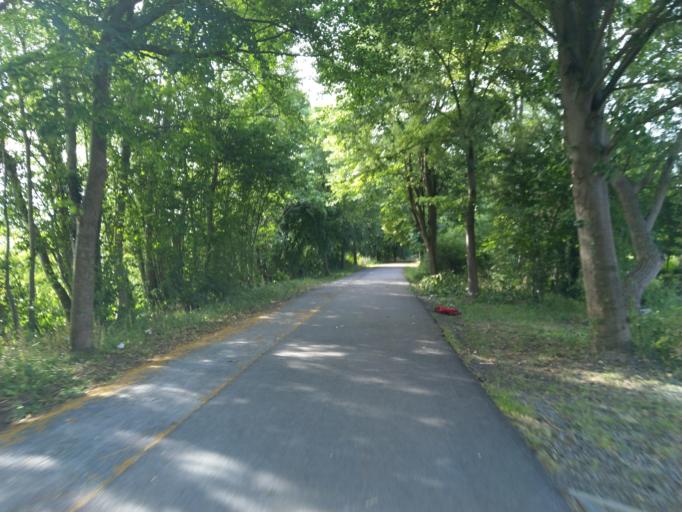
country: BE
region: Wallonia
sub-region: Province du Hainaut
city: Erquelinnes
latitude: 50.3127
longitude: 4.1188
